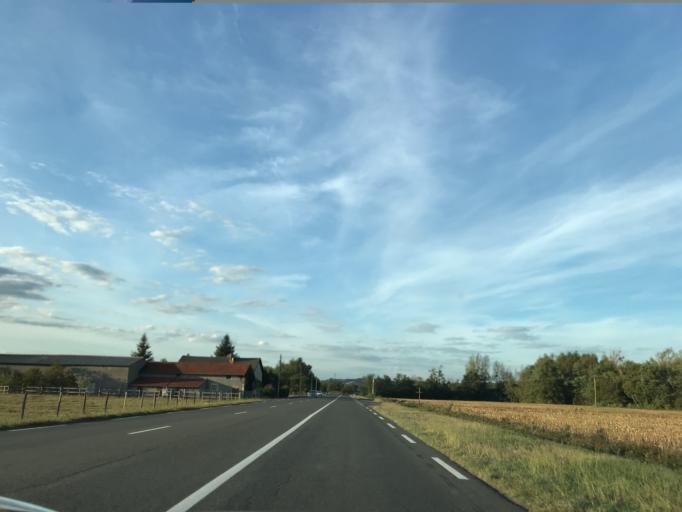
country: FR
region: Auvergne
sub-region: Departement de l'Allier
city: Saint-Yorre
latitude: 46.0359
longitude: 3.4757
